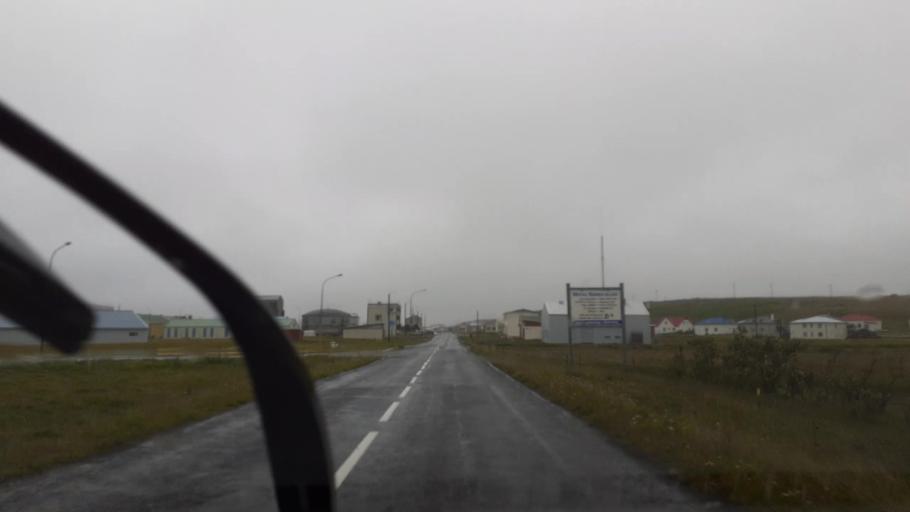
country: IS
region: Northeast
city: Husavik
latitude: 66.4577
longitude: -15.9515
